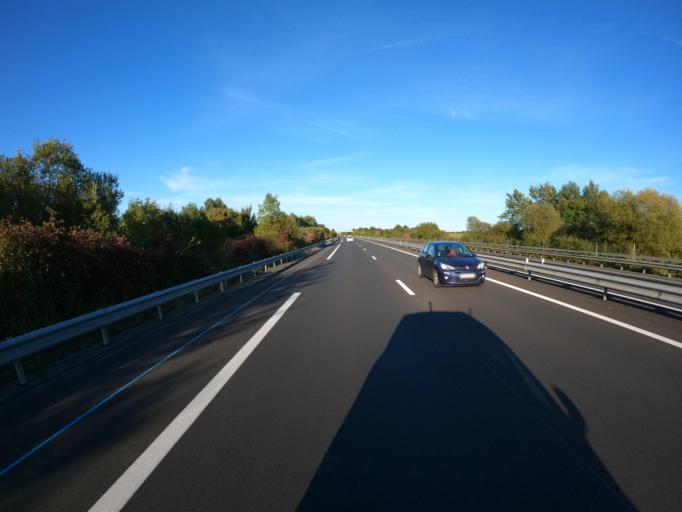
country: FR
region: Pays de la Loire
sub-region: Departement de la Vendee
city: Vendrennes
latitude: 46.8718
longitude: -1.1214
